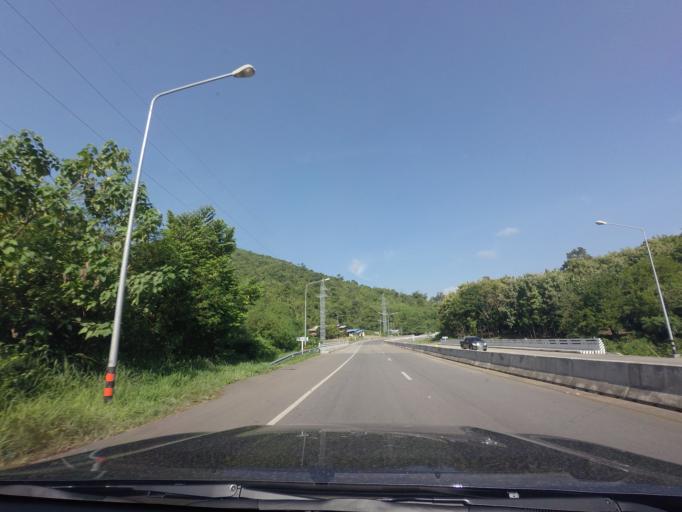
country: TH
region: Phetchabun
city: Lom Sak
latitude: 16.7629
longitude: 101.1419
